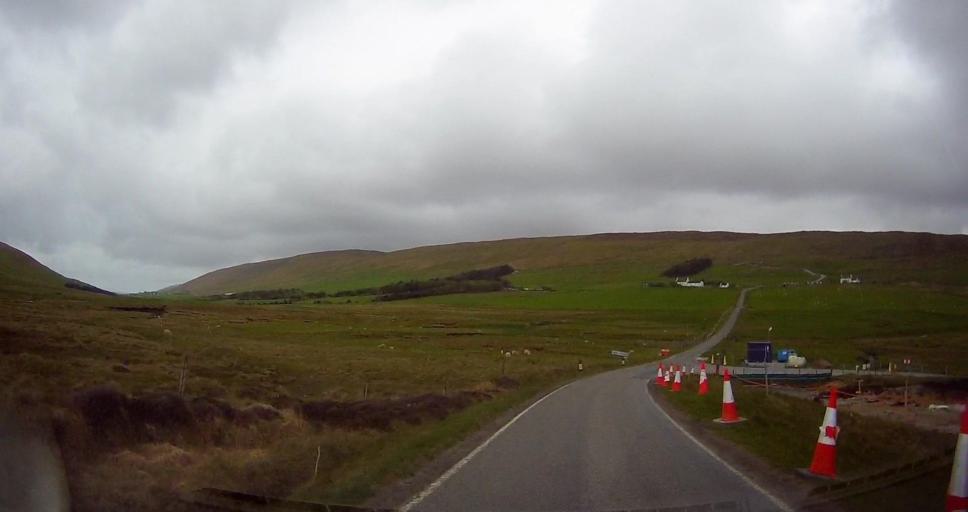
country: GB
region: Scotland
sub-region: Shetland Islands
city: Lerwick
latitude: 60.2760
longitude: -1.2746
